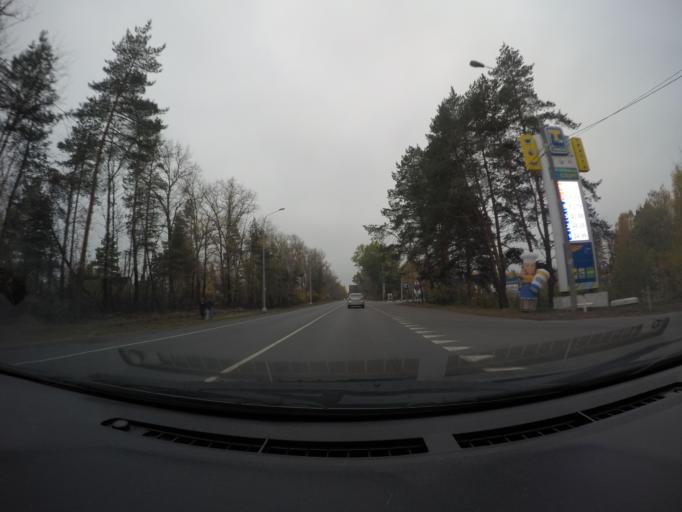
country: RU
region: Moskovskaya
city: Malyshevo
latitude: 55.4727
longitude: 38.3420
